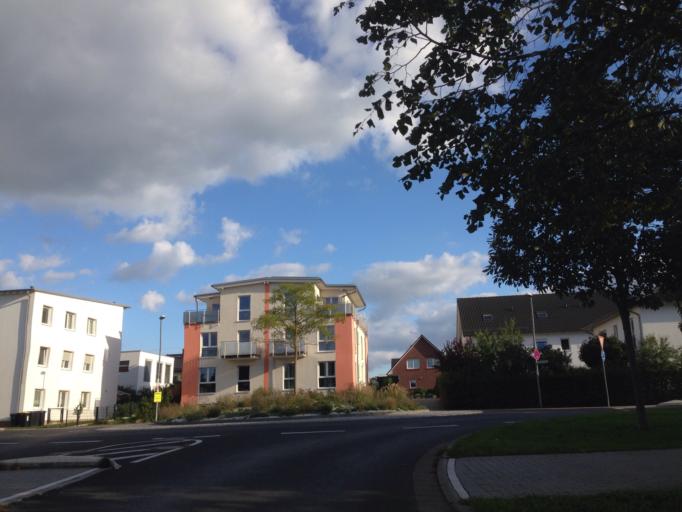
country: DE
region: Hesse
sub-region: Regierungsbezirk Giessen
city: Giessen
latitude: 50.5684
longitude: 8.6679
